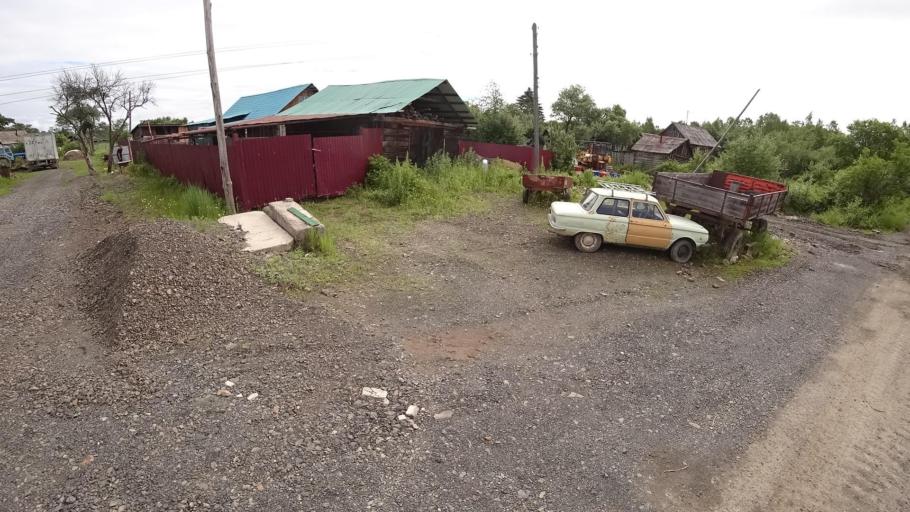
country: RU
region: Khabarovsk Krai
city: Amursk
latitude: 49.9008
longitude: 136.1490
